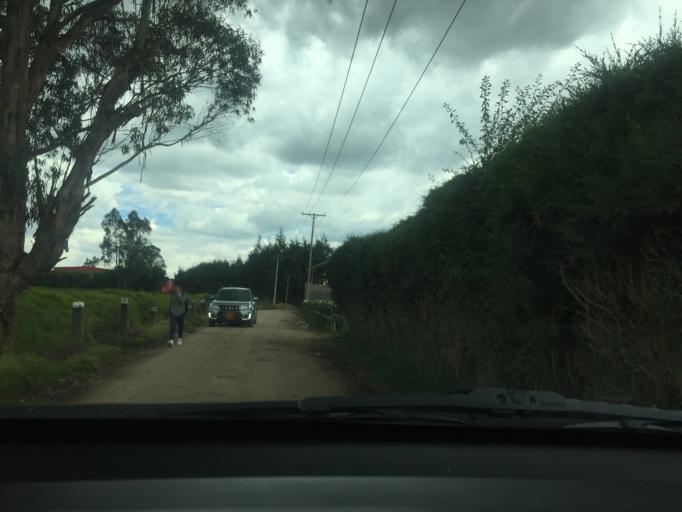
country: CO
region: Cundinamarca
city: Facatativa
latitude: 4.7816
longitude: -74.3158
